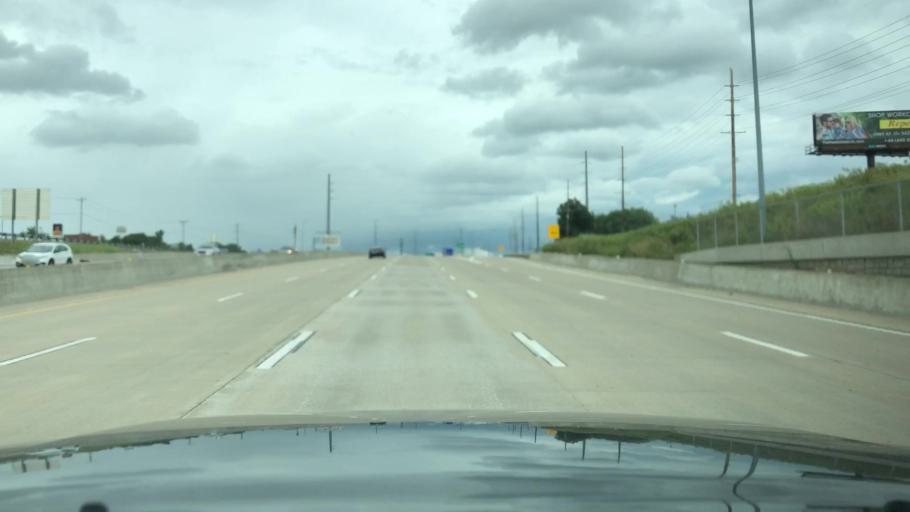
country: US
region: Missouri
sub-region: Saint Charles County
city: Cottleville
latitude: 38.7432
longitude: -90.6058
